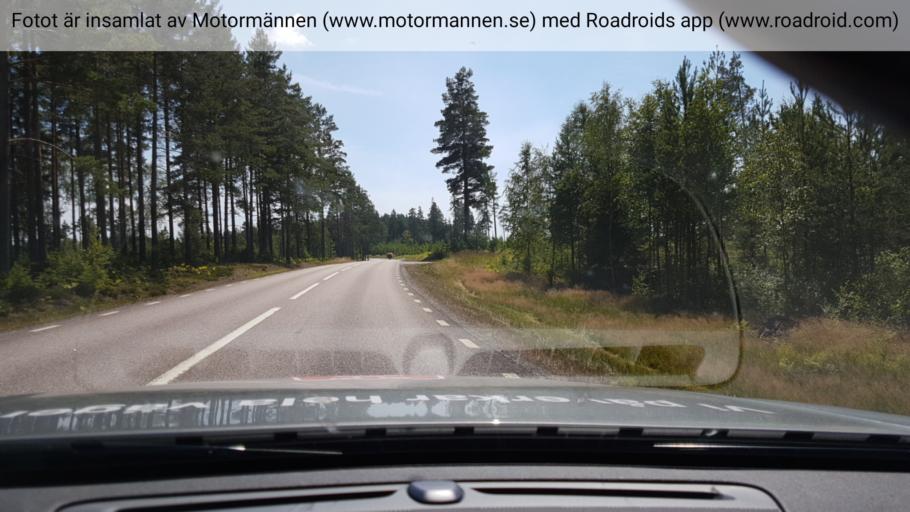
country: SE
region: OErebro
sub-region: Laxa Kommun
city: Laxa
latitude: 58.9201
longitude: 14.6614
